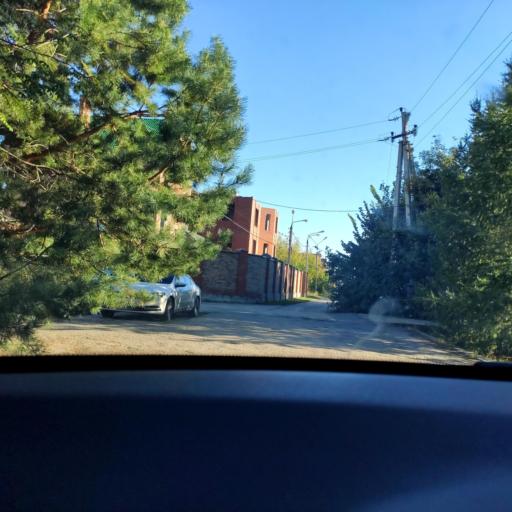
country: RU
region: Samara
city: Samara
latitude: 53.1543
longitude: 50.0822
